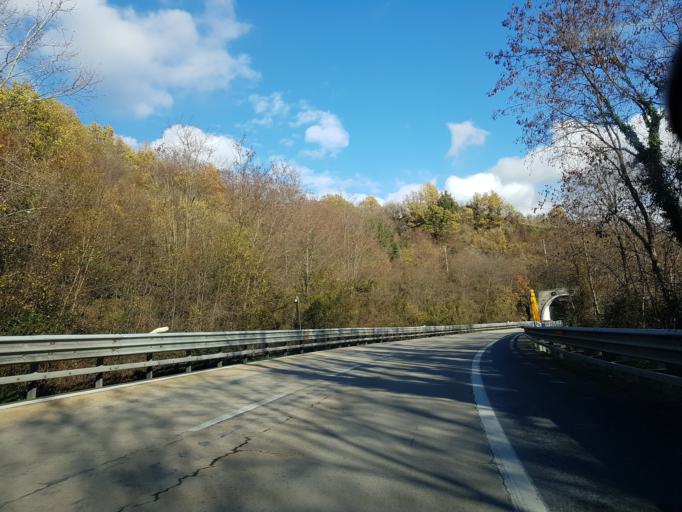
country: IT
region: Liguria
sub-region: Provincia di Genova
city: Pedemonte
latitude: 44.5130
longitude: 8.9278
